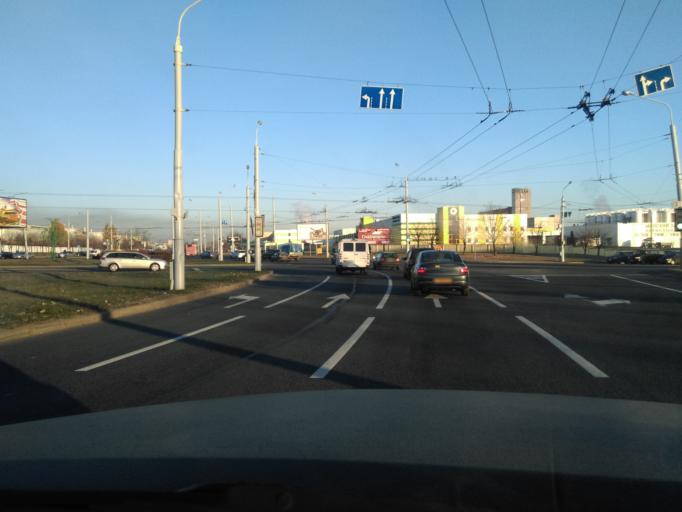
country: BY
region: Minsk
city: Minsk
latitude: 53.8938
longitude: 27.6448
